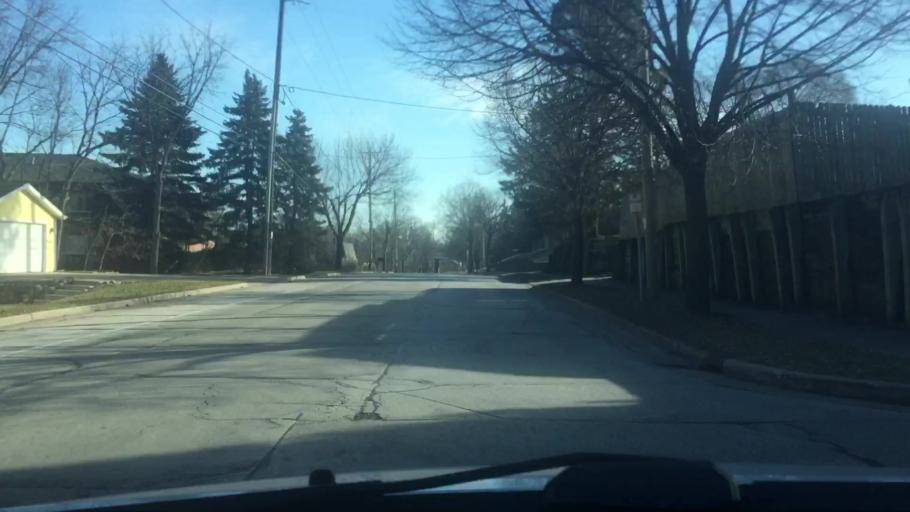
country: US
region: Wisconsin
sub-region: Waukesha County
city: Pewaukee
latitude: 43.0794
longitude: -88.2551
